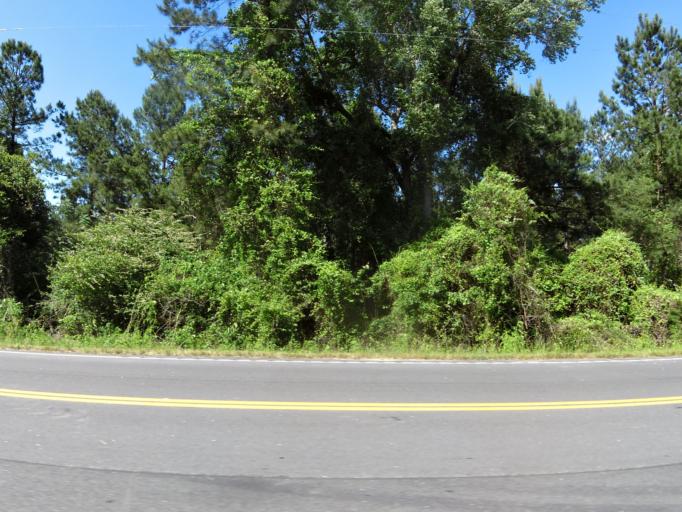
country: US
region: South Carolina
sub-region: Barnwell County
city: Williston
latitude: 33.4158
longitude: -81.4735
